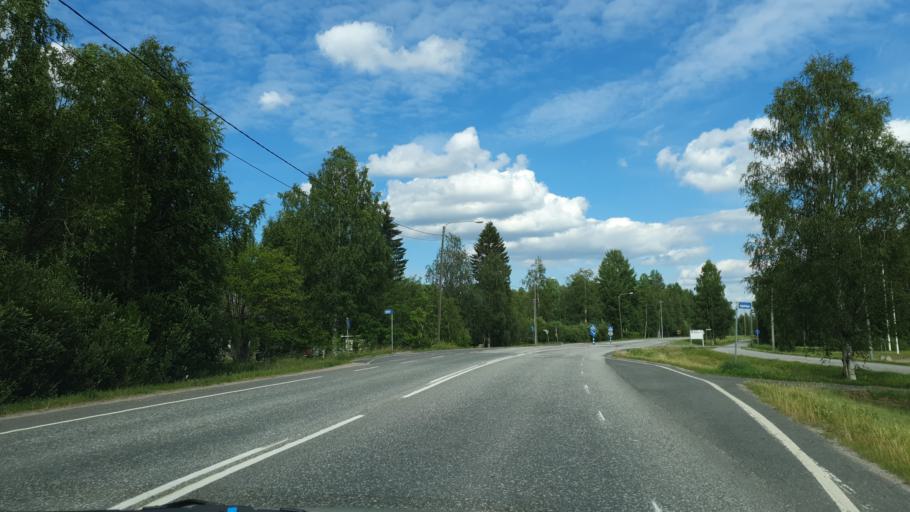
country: FI
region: Kainuu
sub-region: Kajaani
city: Kajaani
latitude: 64.2472
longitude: 27.7662
